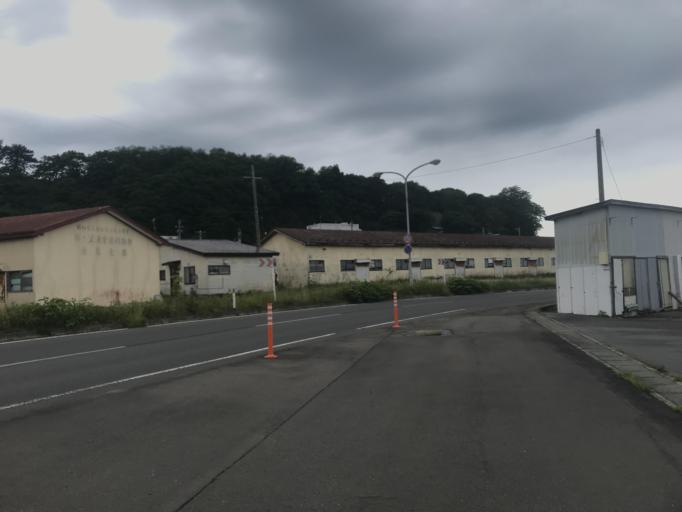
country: JP
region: Aomori
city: Shimokizukuri
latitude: 40.7808
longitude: 140.2076
